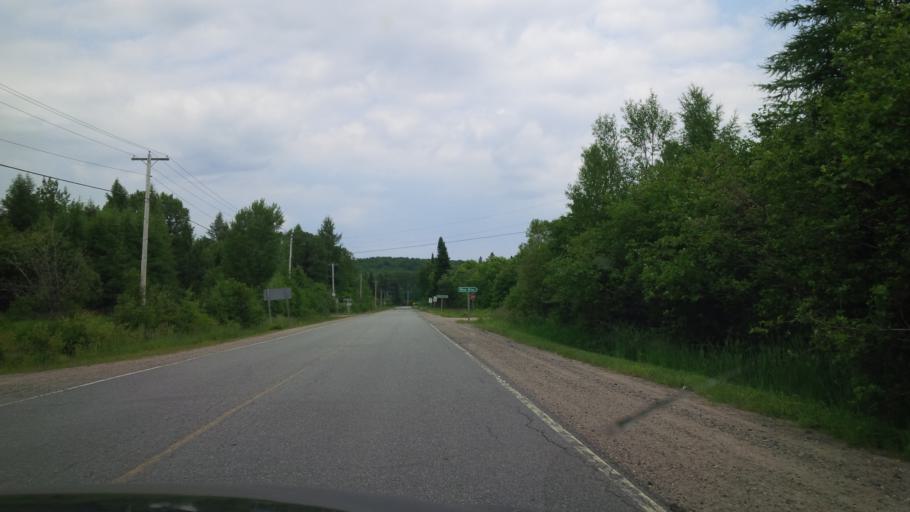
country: CA
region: Ontario
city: Huntsville
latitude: 45.5662
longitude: -79.2260
